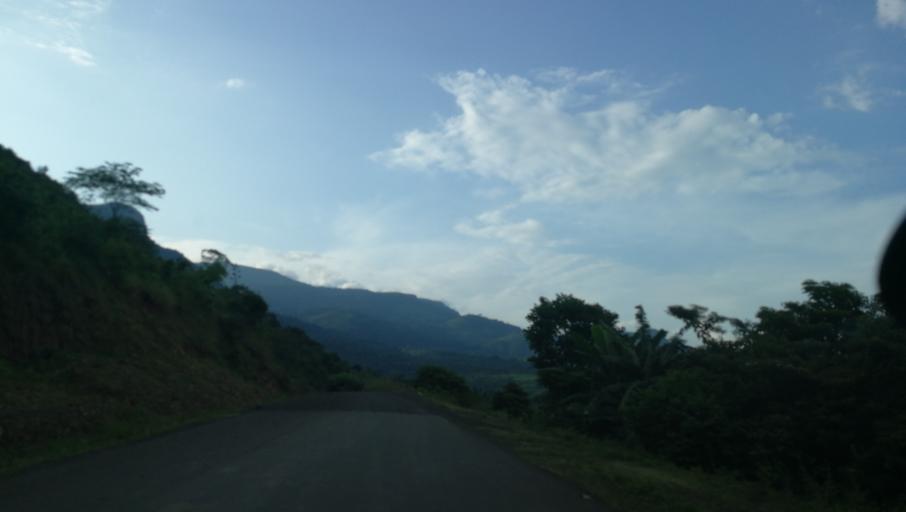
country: ET
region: Southern Nations, Nationalities, and People's Region
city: Areka
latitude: 6.8563
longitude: 37.2645
